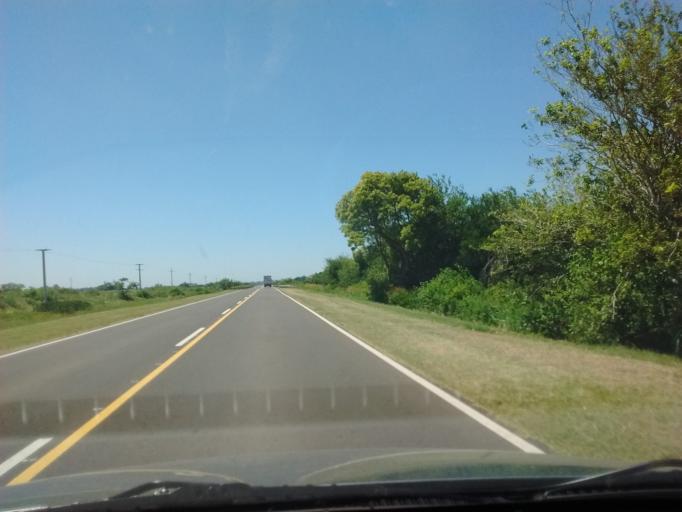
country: AR
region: Entre Rios
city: General Galarza
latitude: -32.8842
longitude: -59.7027
